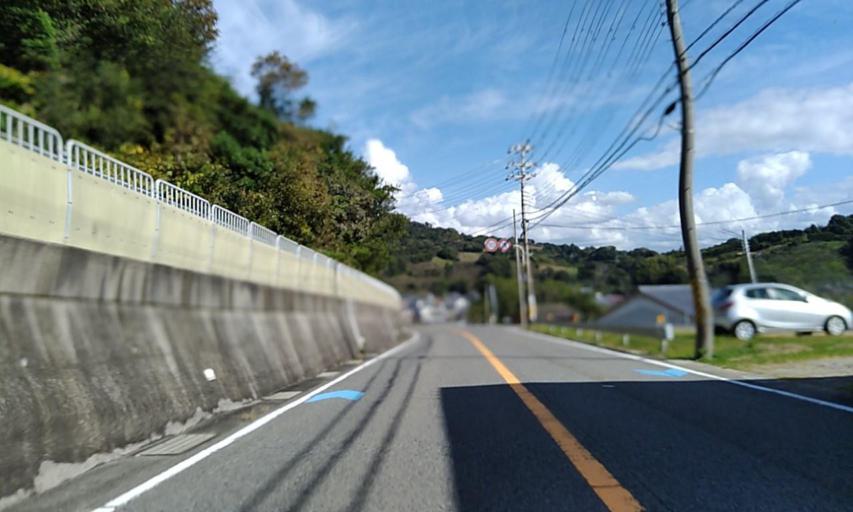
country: JP
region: Wakayama
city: Tanabe
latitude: 33.7820
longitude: 135.2817
